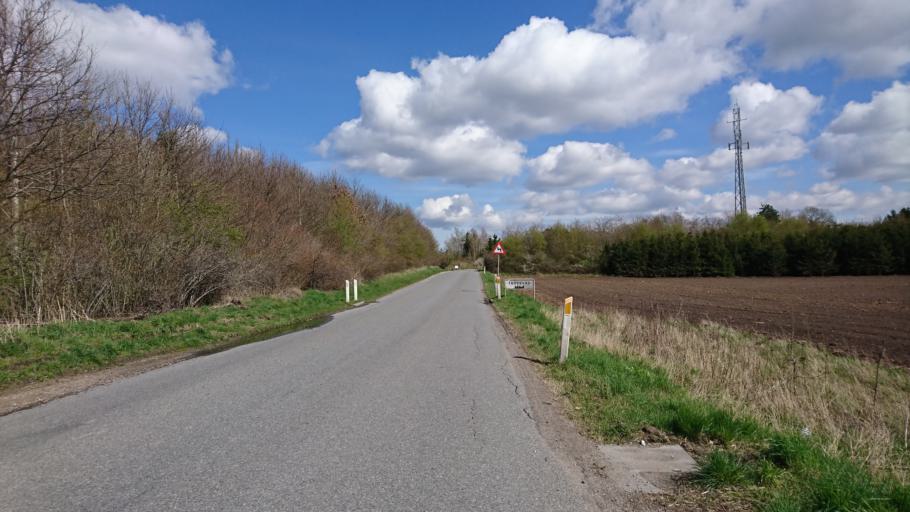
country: DK
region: Capital Region
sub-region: Egedal Kommune
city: Ganlose
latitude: 55.7792
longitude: 12.2654
